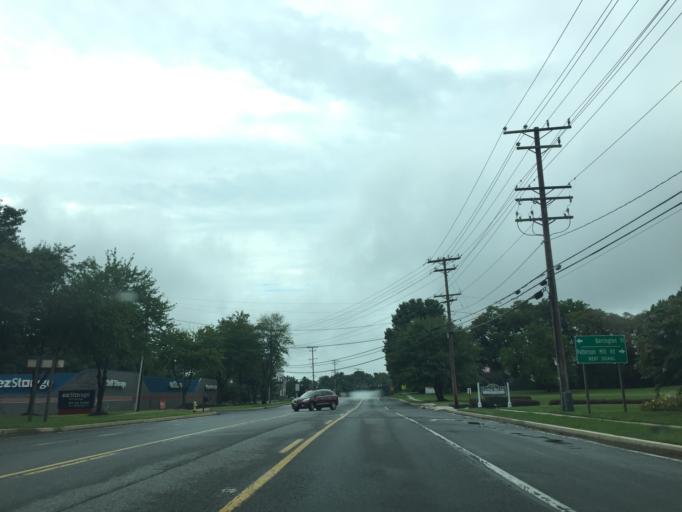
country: US
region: Maryland
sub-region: Harford County
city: Bel Air South
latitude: 39.5037
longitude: -76.3272
